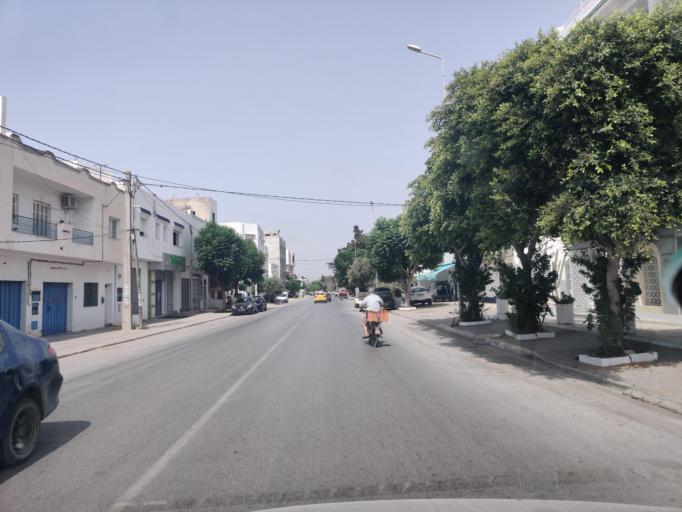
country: TN
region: Nabul
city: Al Hammamat
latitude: 36.4090
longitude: 10.6054
